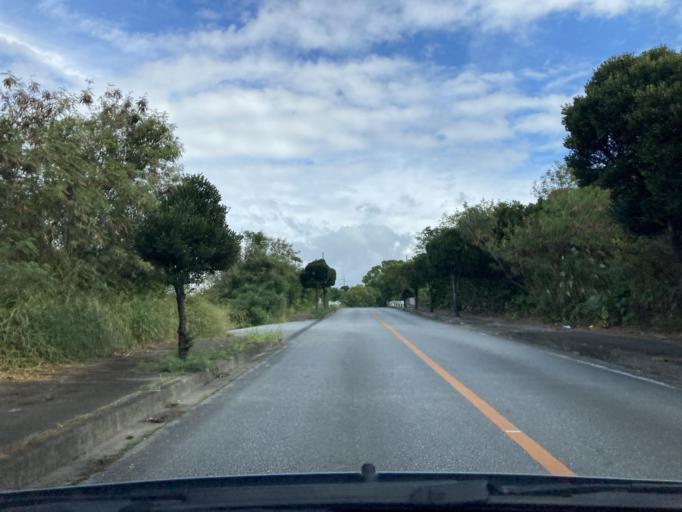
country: JP
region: Okinawa
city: Itoman
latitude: 26.1313
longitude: 127.7079
